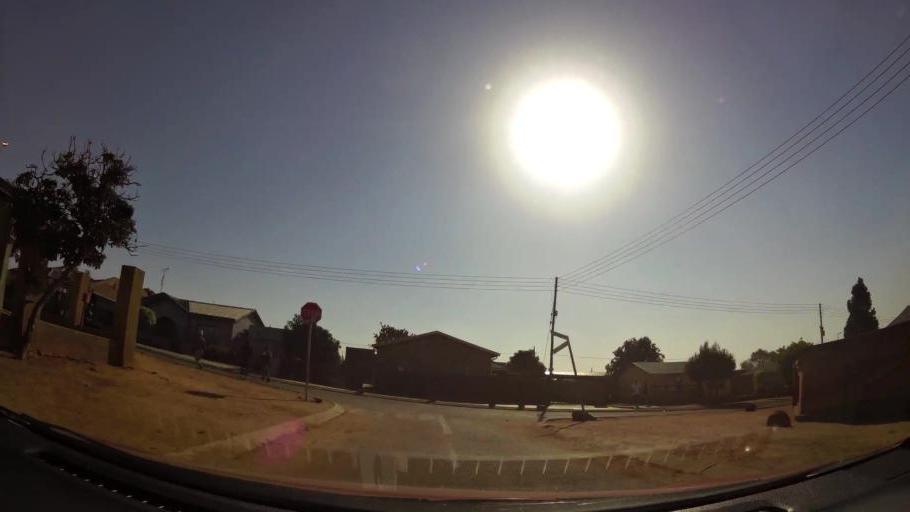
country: ZA
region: Gauteng
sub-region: City of Tshwane Metropolitan Municipality
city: Mabopane
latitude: -25.5272
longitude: 28.1070
